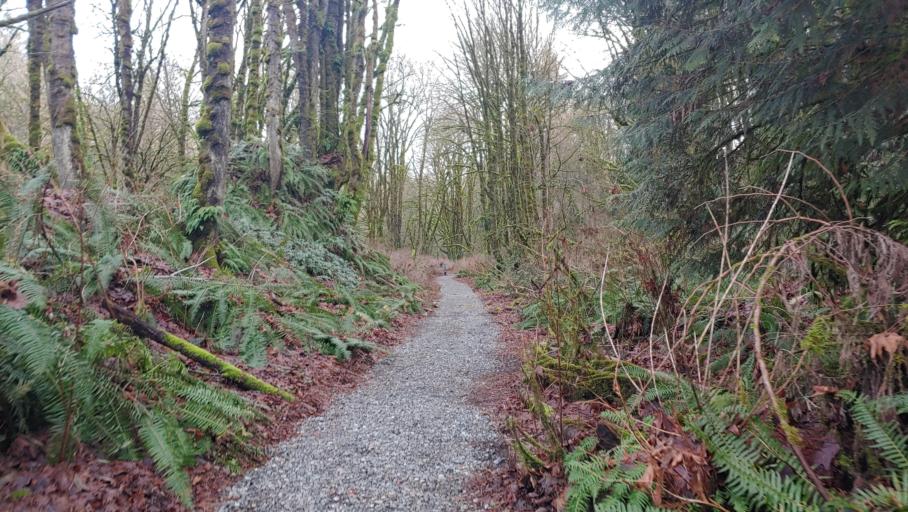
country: US
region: Washington
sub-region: King County
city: Newcastle
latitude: 47.5396
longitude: -122.1360
